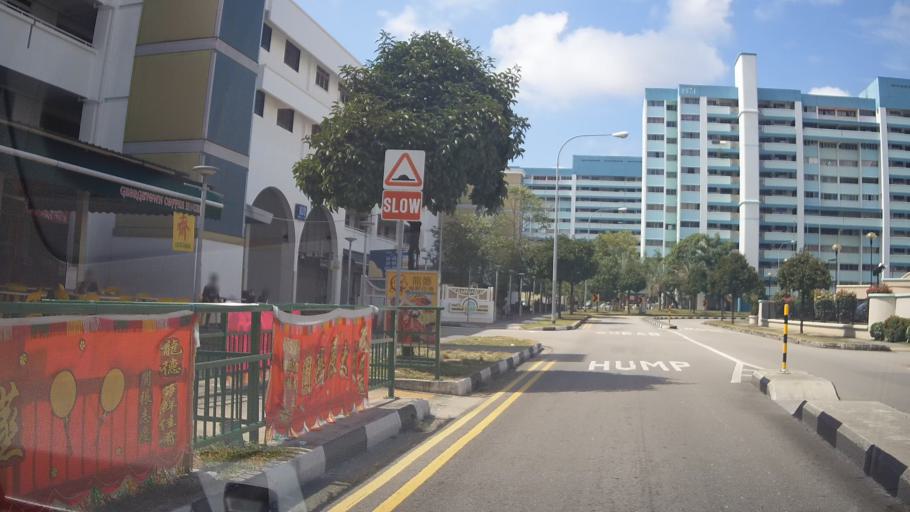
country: SG
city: Singapore
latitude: 1.3485
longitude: 103.9362
